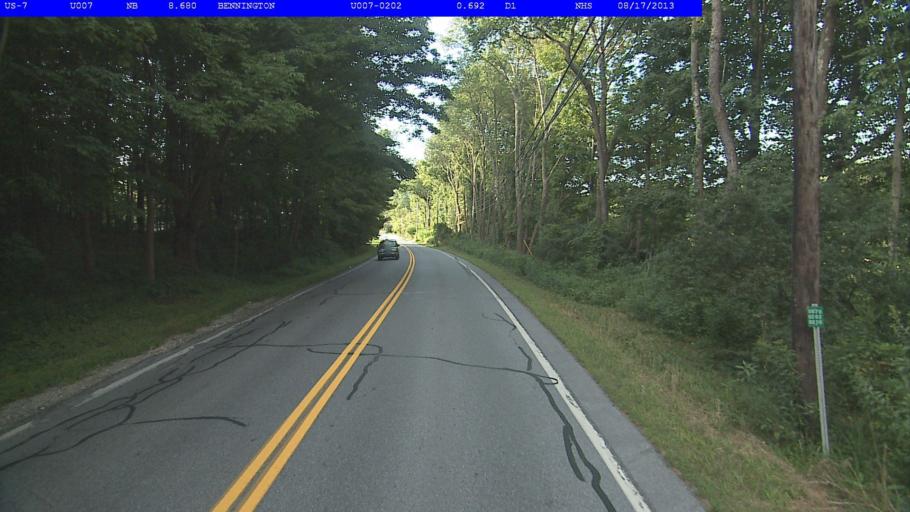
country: US
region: Vermont
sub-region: Bennington County
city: Bennington
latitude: 42.8472
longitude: -73.2021
